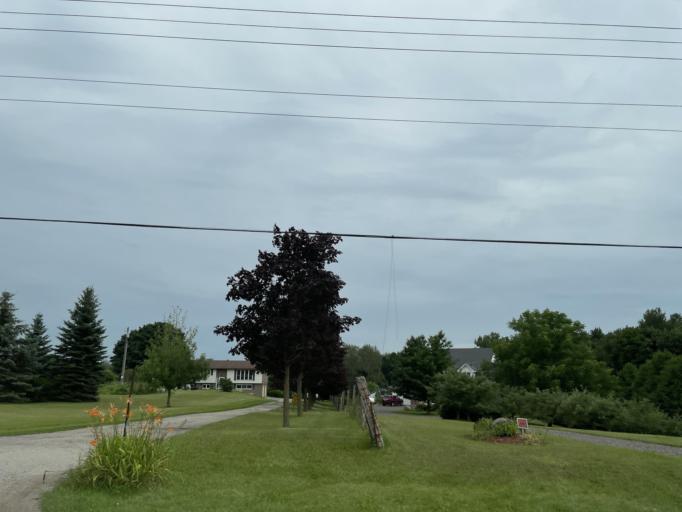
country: CA
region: Ontario
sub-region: Wellington County
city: Guelph
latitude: 43.5730
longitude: -80.3172
